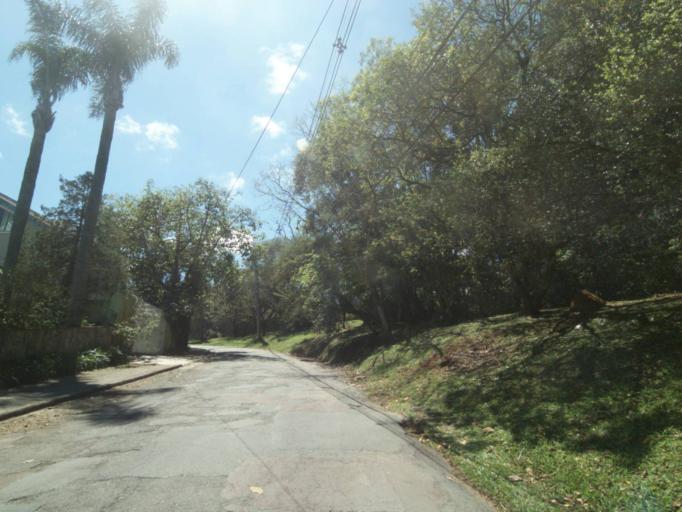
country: BR
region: Parana
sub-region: Curitiba
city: Curitiba
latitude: -25.3813
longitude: -49.2651
